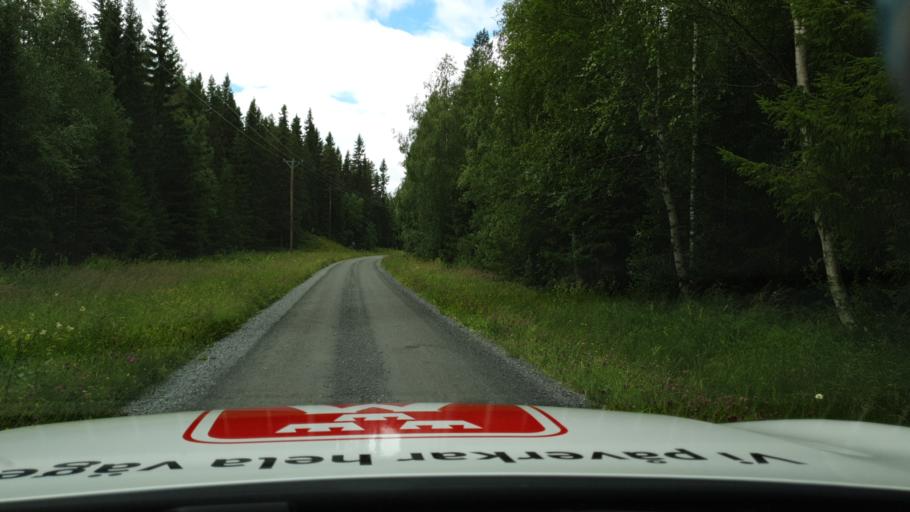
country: SE
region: Jaemtland
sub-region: Krokoms Kommun
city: Krokom
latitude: 63.3471
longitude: 14.2978
